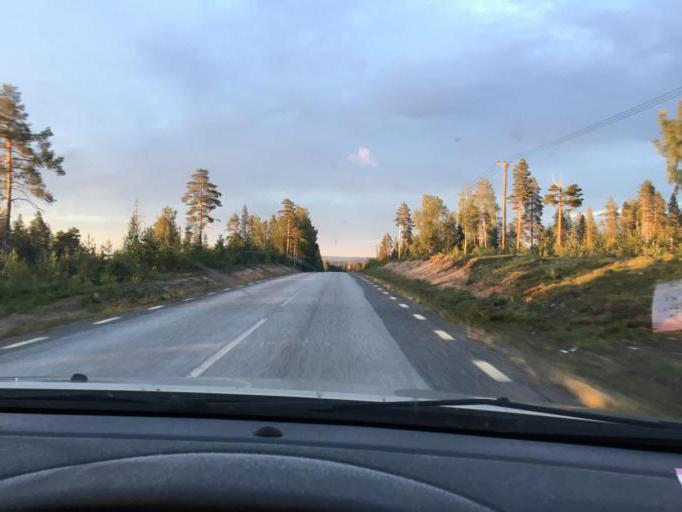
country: SE
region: Norrbotten
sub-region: Kalix Kommun
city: Toere
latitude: 66.0635
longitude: 22.6308
